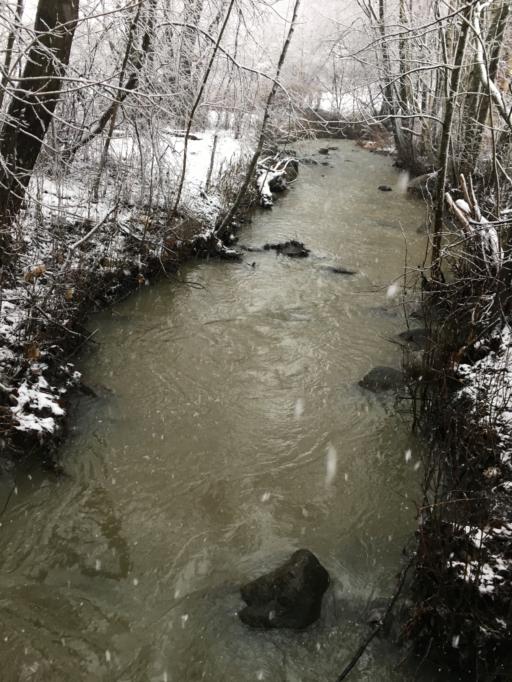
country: FI
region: Uusimaa
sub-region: Helsinki
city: Vantaa
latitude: 60.2437
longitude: 25.0088
